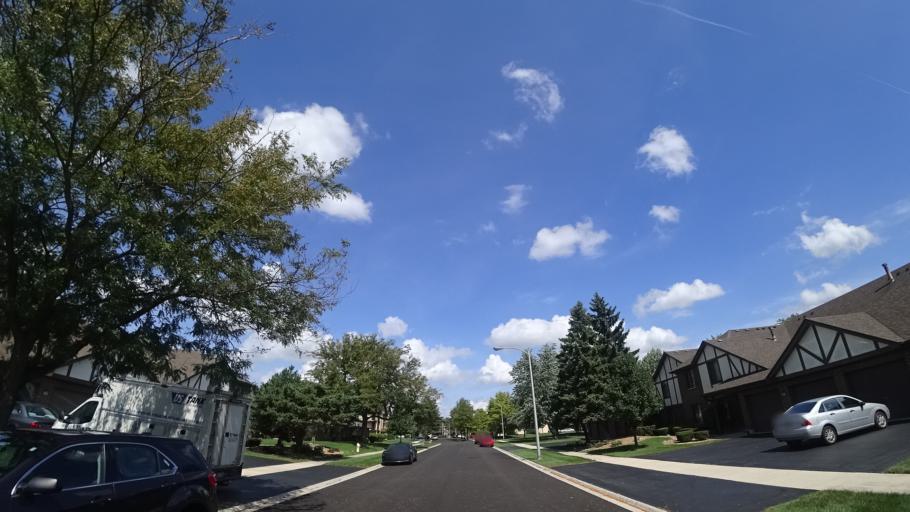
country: US
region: Illinois
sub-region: Cook County
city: Tinley Park
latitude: 41.5629
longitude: -87.7810
